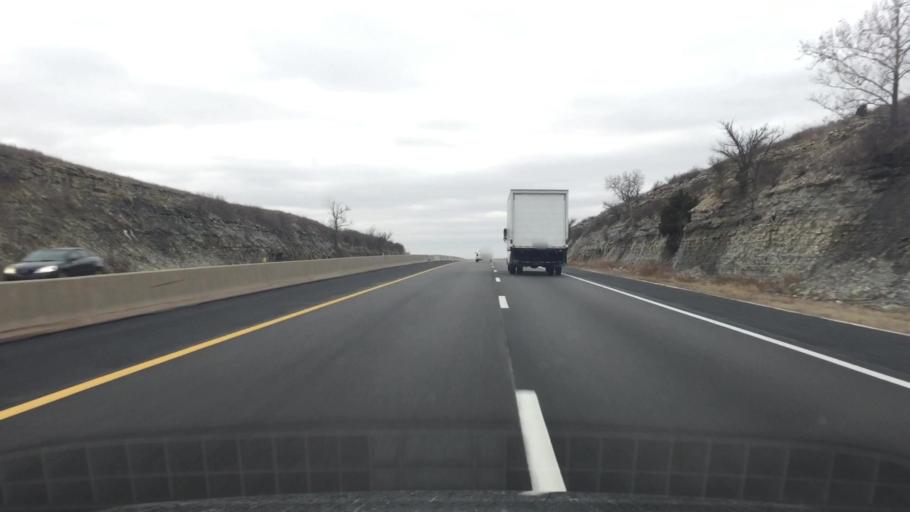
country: US
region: Kansas
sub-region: Chase County
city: Cottonwood Falls
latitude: 38.1360
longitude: -96.5332
